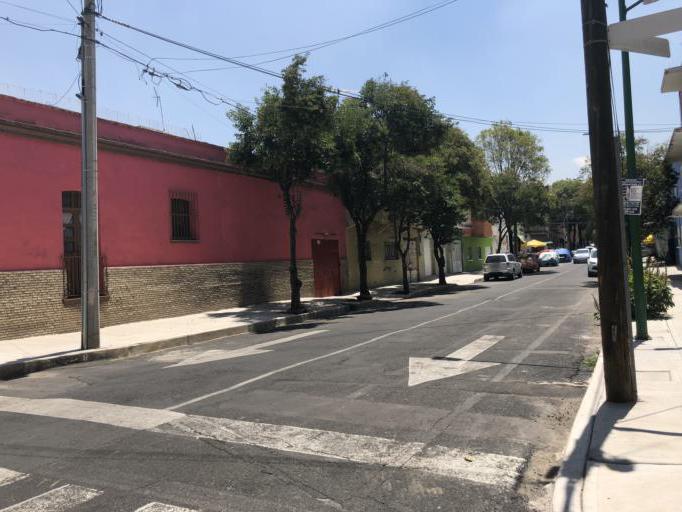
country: MX
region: Mexico City
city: Cuauhtemoc
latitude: 19.4562
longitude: -99.1345
